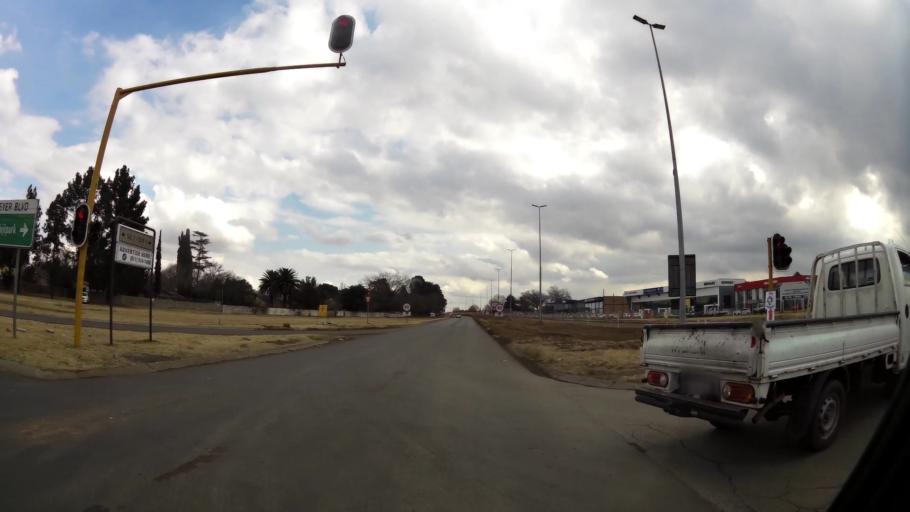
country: ZA
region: Gauteng
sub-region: Sedibeng District Municipality
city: Vanderbijlpark
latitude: -26.7063
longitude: 27.8358
